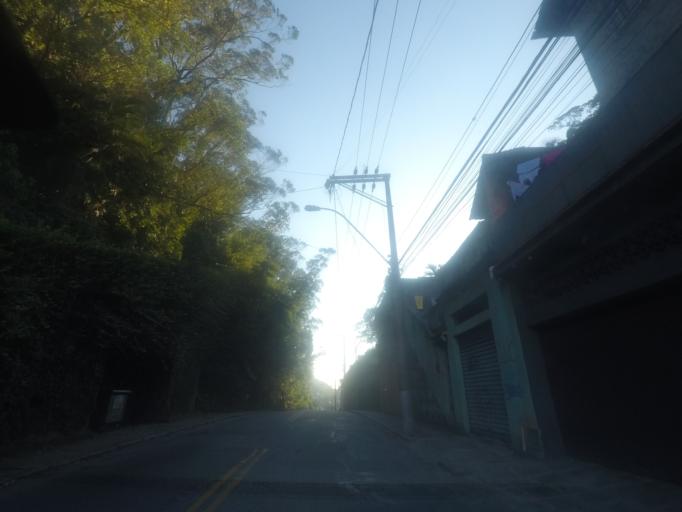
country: BR
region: Rio de Janeiro
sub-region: Petropolis
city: Petropolis
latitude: -22.5302
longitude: -43.1921
